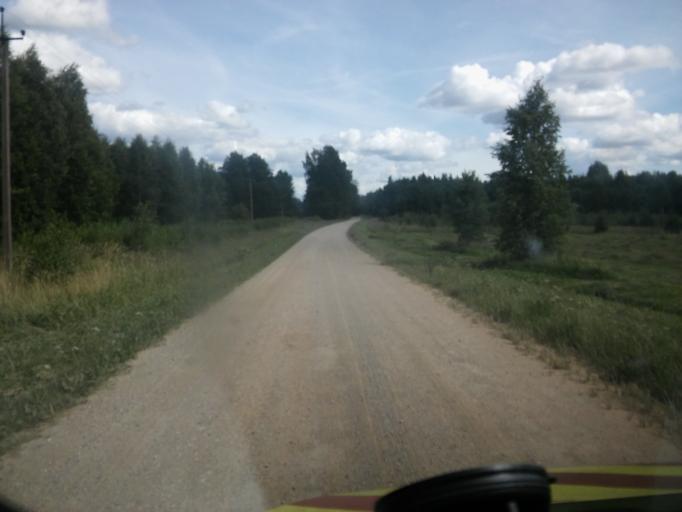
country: EE
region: Viljandimaa
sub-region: Karksi vald
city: Karksi-Nuia
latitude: 58.0860
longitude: 25.4999
